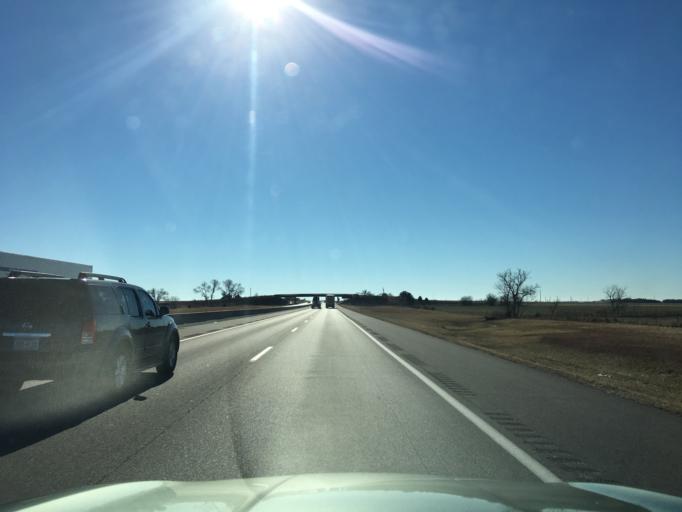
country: US
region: Kansas
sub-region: Sumner County
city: Wellington
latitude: 37.3083
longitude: -97.3406
